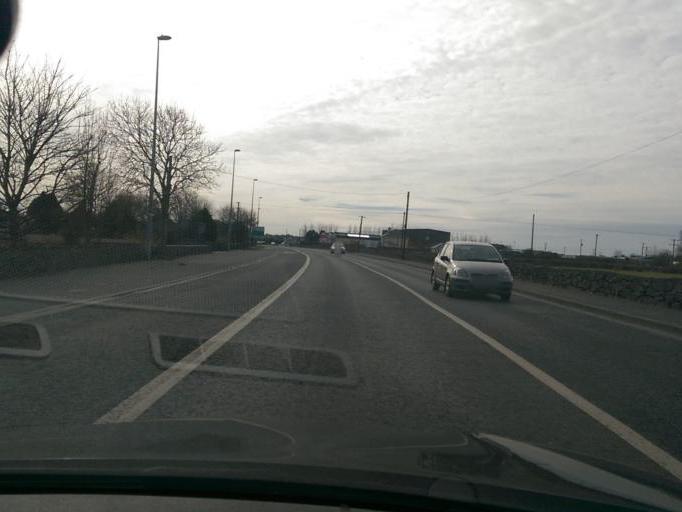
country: IE
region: Connaught
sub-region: County Galway
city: Claregalway
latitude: 53.3518
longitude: -8.9367
